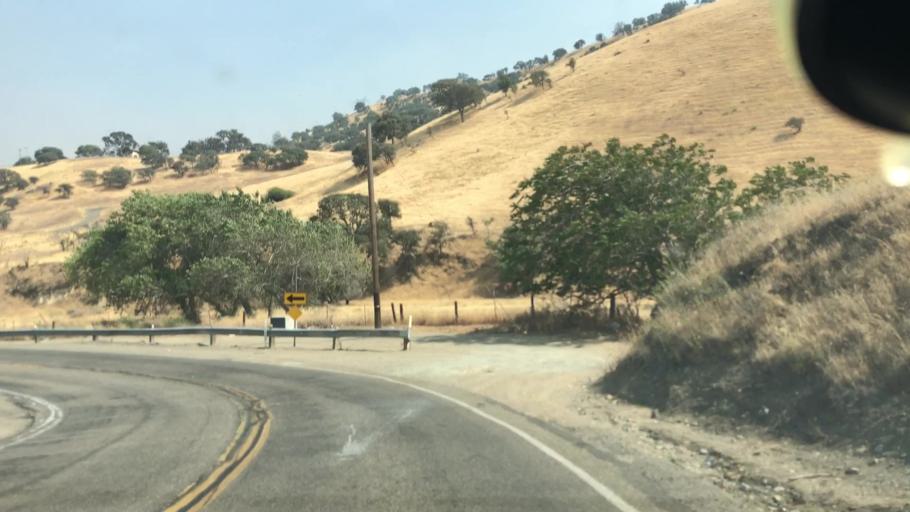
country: US
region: California
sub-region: San Joaquin County
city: Mountain House
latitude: 37.6406
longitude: -121.5939
